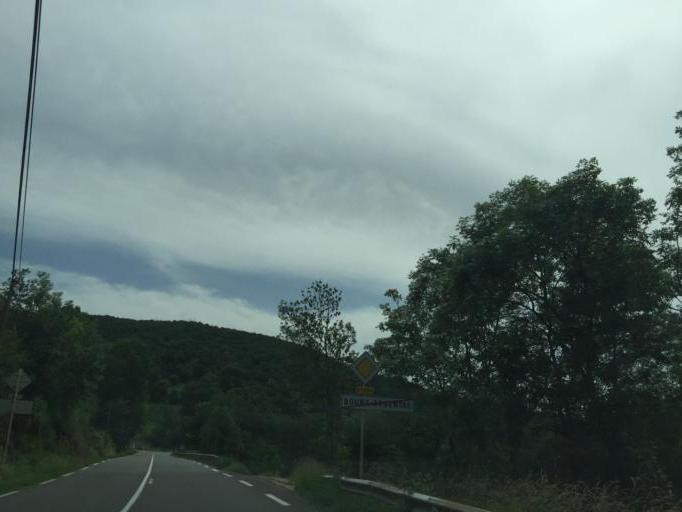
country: FR
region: Rhone-Alpes
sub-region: Departement de la Loire
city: Bourg-Argental
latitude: 45.2993
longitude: 4.5857
